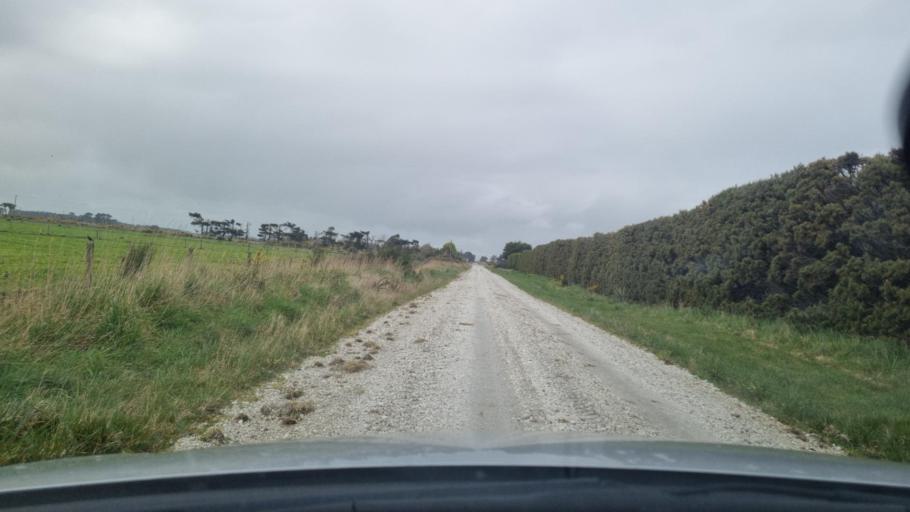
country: NZ
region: Southland
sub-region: Invercargill City
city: Invercargill
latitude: -46.4977
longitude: 168.4157
